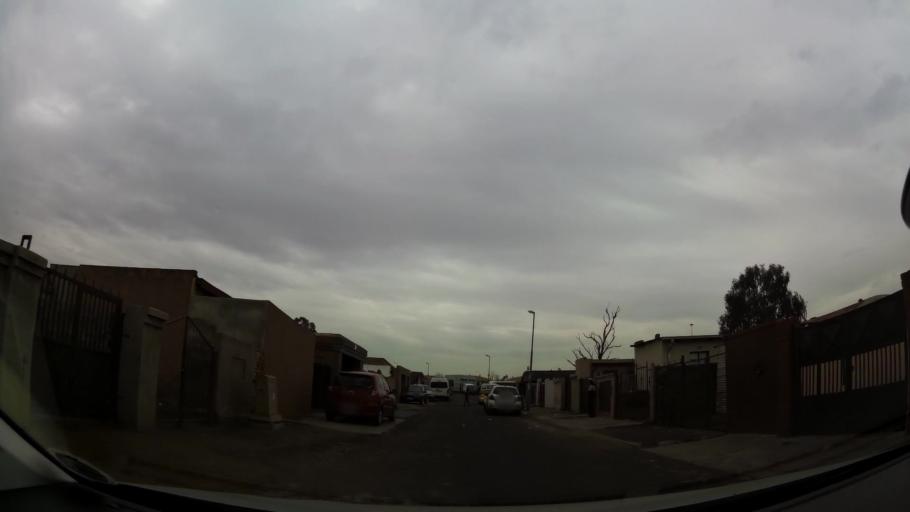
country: ZA
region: Gauteng
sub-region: City of Johannesburg Metropolitan Municipality
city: Soweto
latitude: -26.2550
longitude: 27.8761
